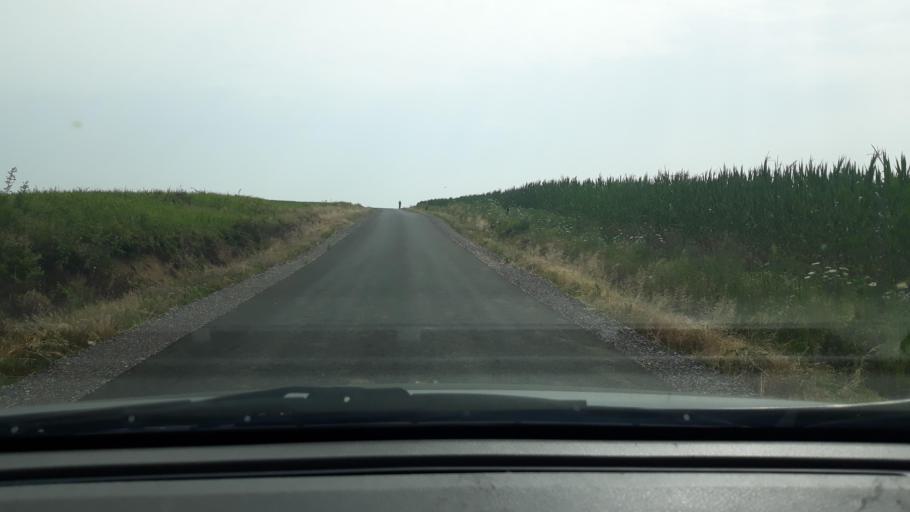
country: RO
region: Bihor
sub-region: Comuna Chislaz
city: Misca
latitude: 47.2766
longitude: 22.2744
